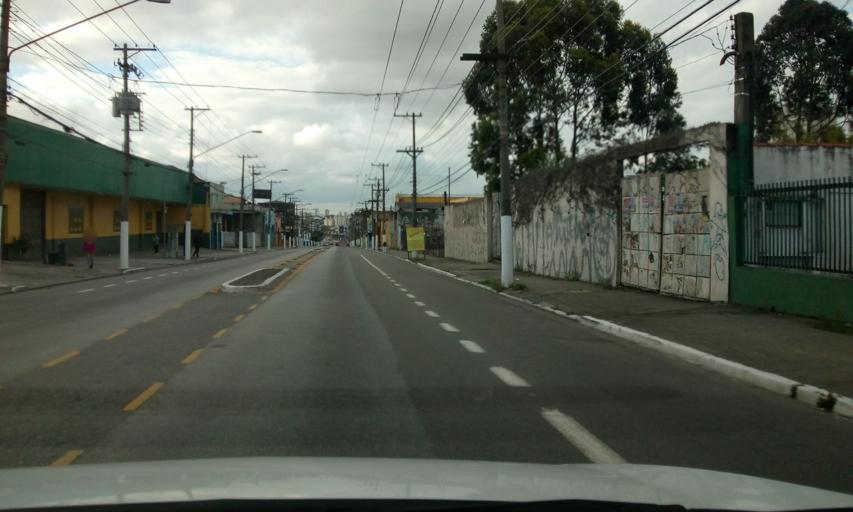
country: BR
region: Sao Paulo
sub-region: Sao Caetano Do Sul
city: Sao Caetano do Sul
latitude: -23.5762
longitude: -46.5039
